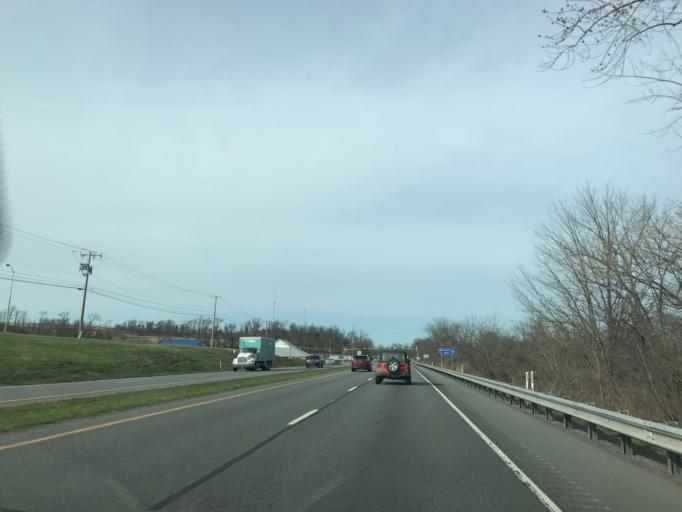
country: US
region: Pennsylvania
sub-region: Union County
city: Lewisburg
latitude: 40.9924
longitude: -76.8738
